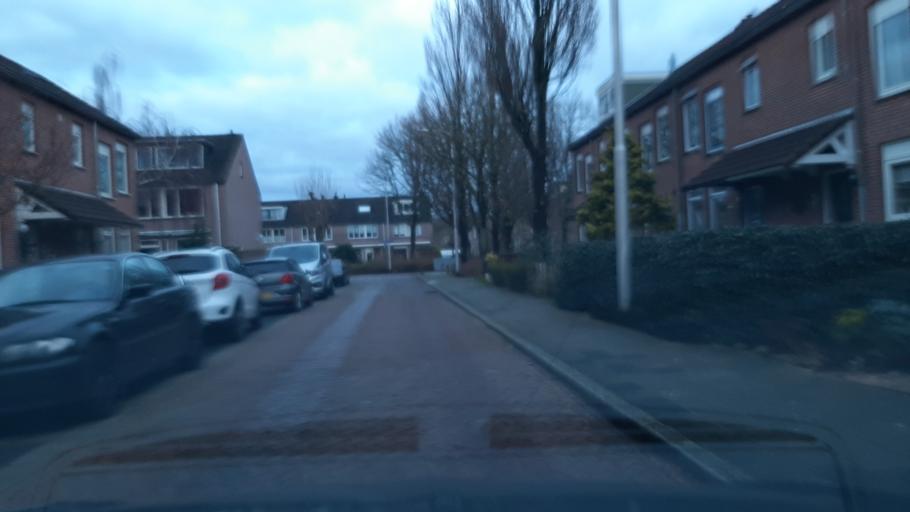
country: NL
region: South Holland
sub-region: Gemeente Hillegom
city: Hillegom
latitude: 52.2841
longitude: 4.5860
